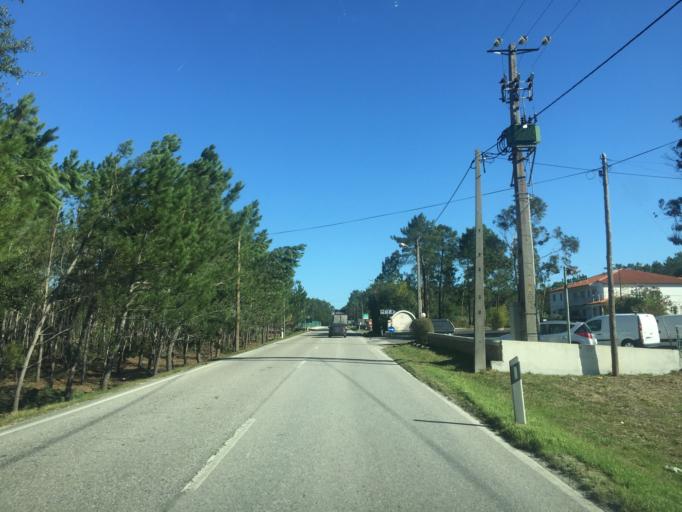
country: PT
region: Leiria
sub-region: Leiria
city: Monte Redondo
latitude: 39.9214
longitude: -8.8105
